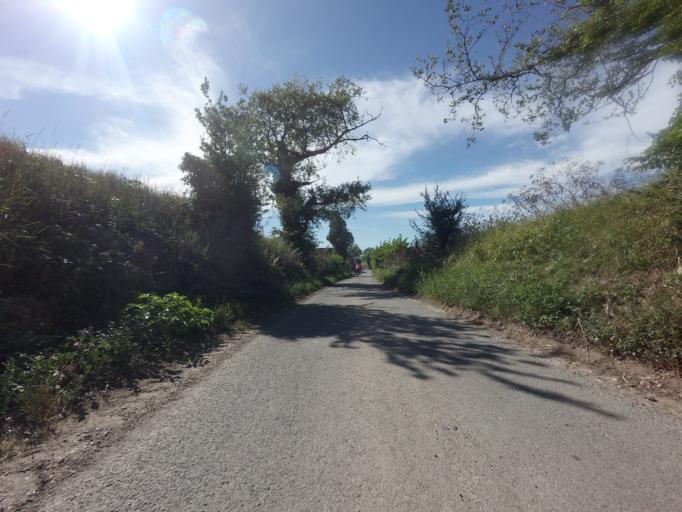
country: GB
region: England
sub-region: Kent
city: Birchington-on-Sea
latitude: 51.3625
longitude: 1.2389
